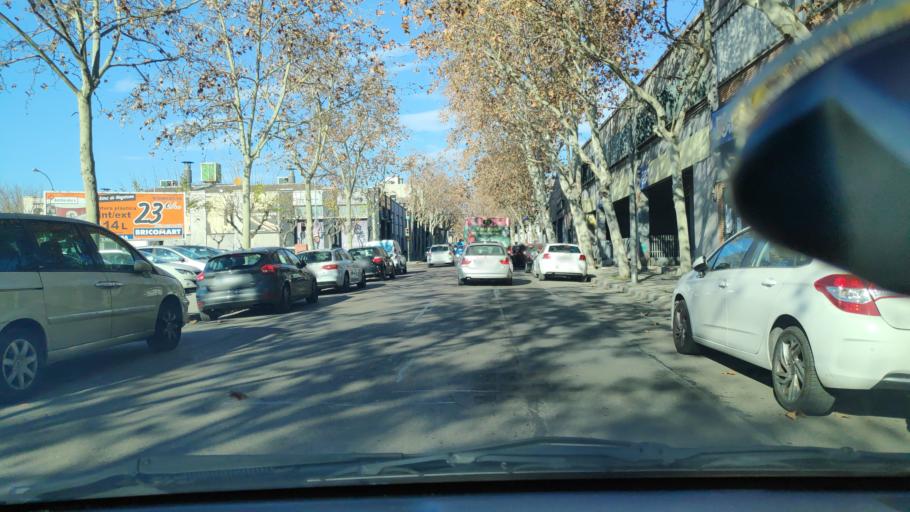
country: ES
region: Catalonia
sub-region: Provincia de Barcelona
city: Sabadell
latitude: 41.5338
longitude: 2.0996
